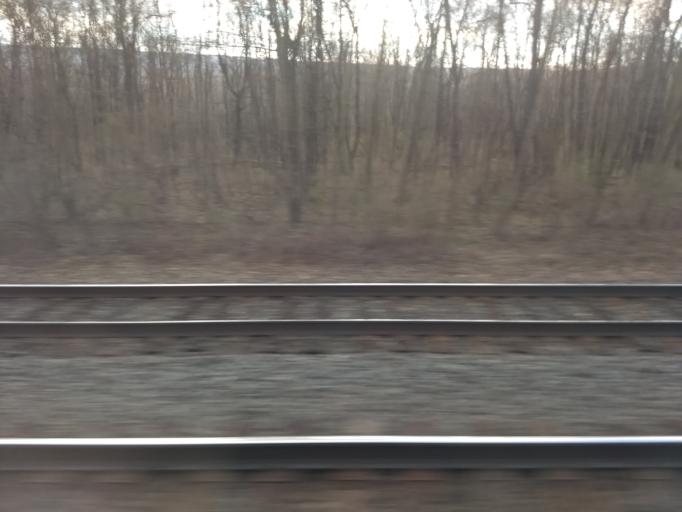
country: US
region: Pennsylvania
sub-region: Blair County
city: Bellwood
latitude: 40.5862
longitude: -78.3460
